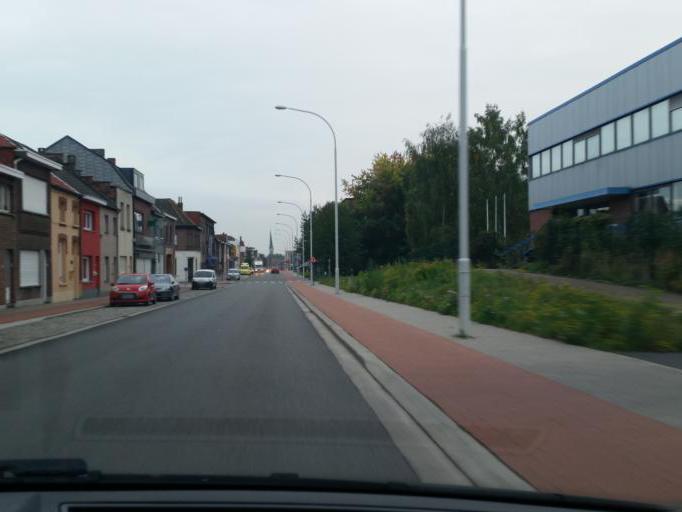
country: BE
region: Flanders
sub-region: Provincie Antwerpen
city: Hemiksem
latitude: 51.1367
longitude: 4.3350
